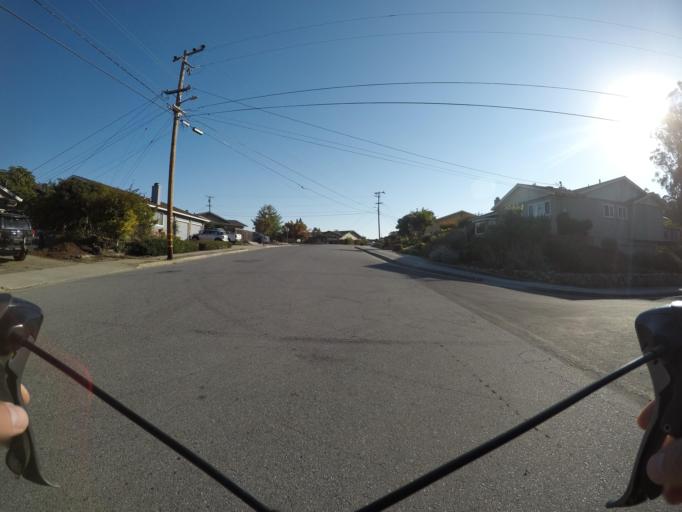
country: US
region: California
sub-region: Santa Cruz County
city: Live Oak
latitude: 37.0021
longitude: -121.9764
